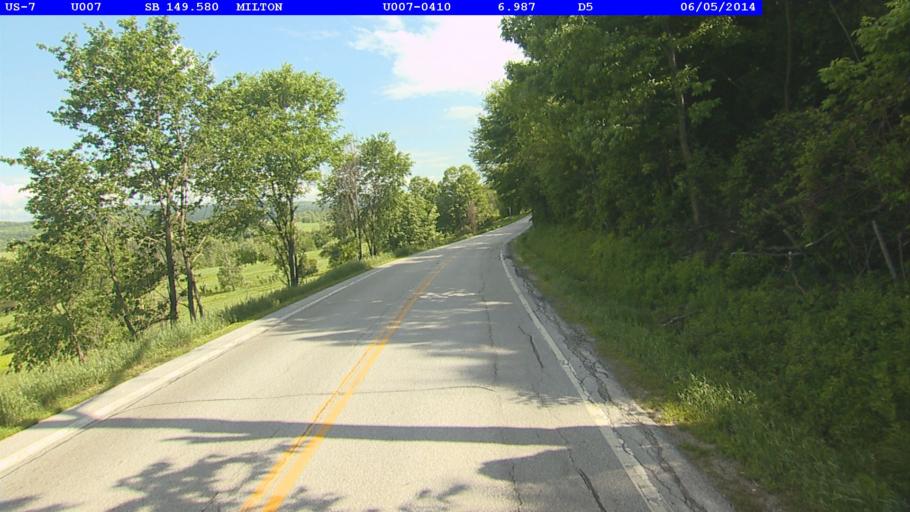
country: US
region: Vermont
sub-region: Chittenden County
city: Milton
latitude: 44.6671
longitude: -73.1114
